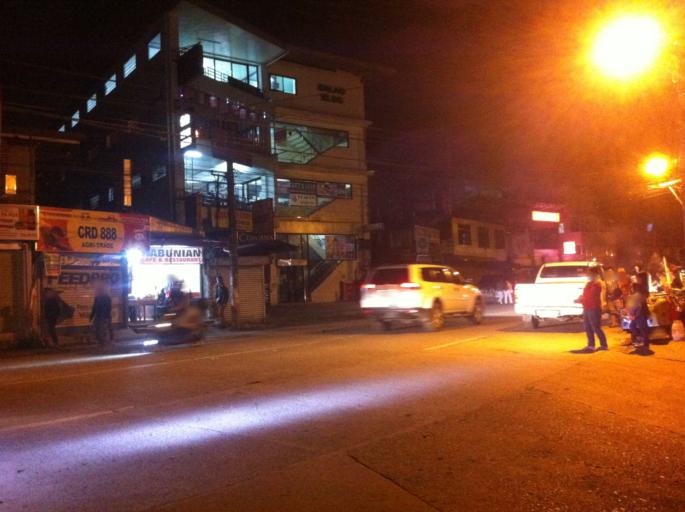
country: PH
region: Cordillera
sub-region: Province of Benguet
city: La Trinidad
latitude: 16.4475
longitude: 120.5899
